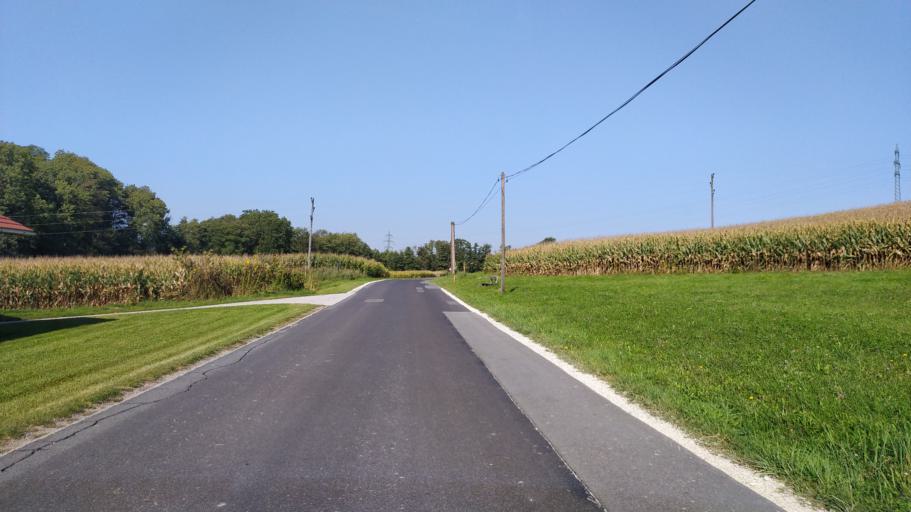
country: AT
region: Lower Austria
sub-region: Politischer Bezirk Amstetten
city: Zeillern
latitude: 48.1114
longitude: 14.7479
